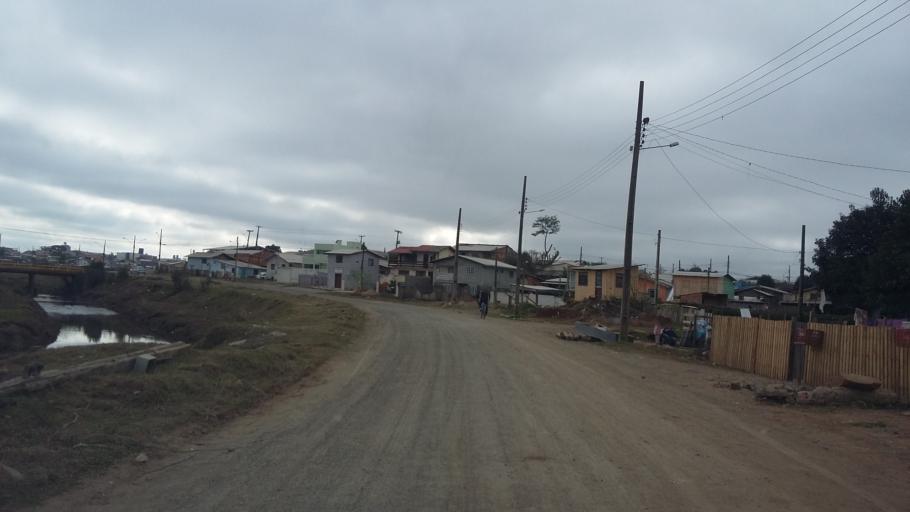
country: BR
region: Santa Catarina
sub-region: Lages
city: Lages
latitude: -27.8353
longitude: -50.3211
